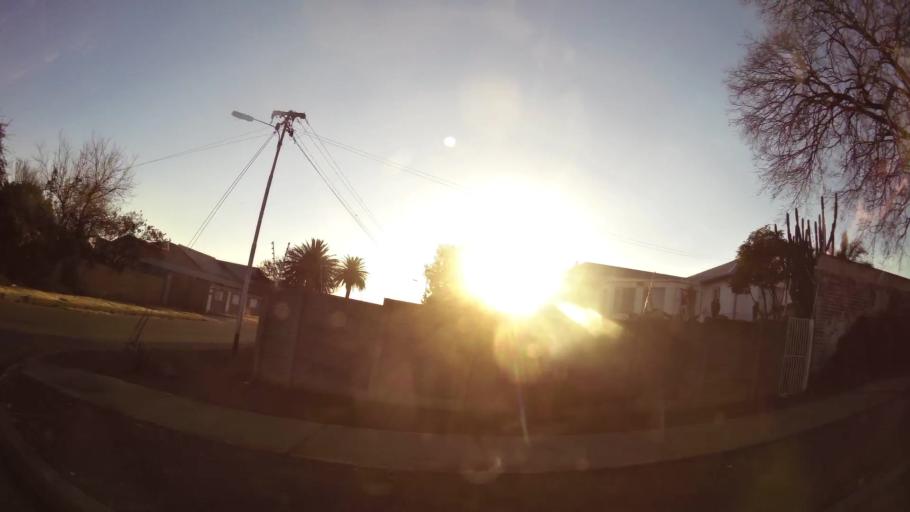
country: ZA
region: Gauteng
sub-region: City of Johannesburg Metropolitan Municipality
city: Roodepoort
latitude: -26.1777
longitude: 27.9422
